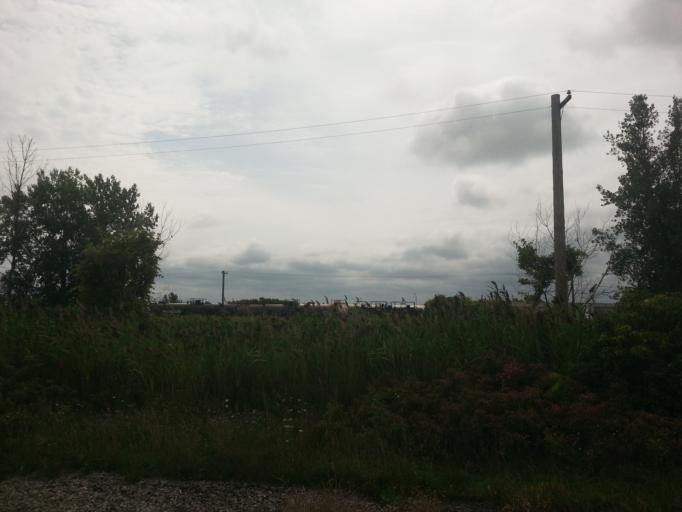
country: US
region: New York
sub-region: Niagara County
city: Niagara Falls
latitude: 43.1143
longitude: -79.0268
